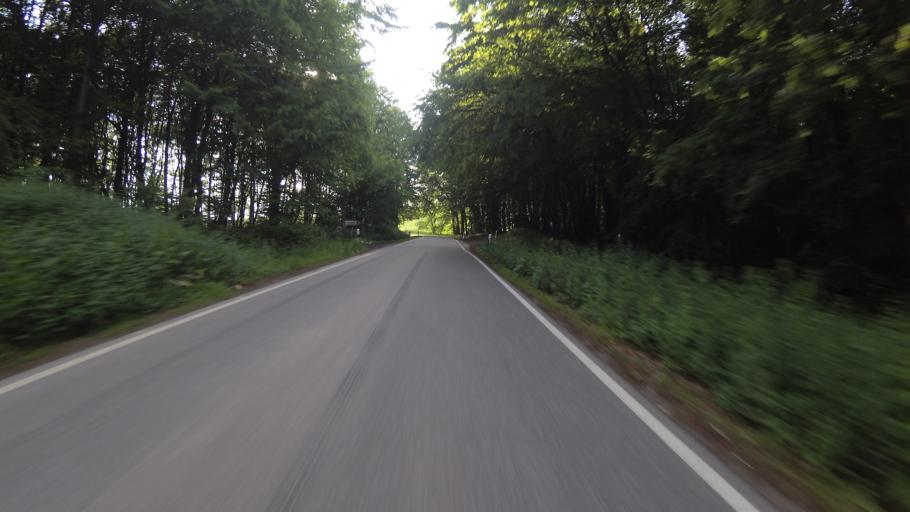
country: DE
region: Rheinland-Pfalz
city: Frohnhofen
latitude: 49.4686
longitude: 7.3014
